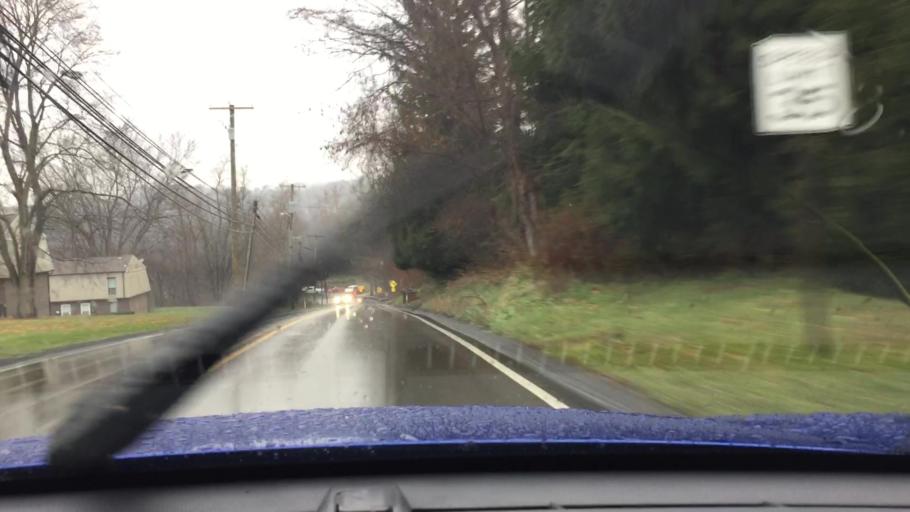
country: US
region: Pennsylvania
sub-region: Washington County
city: Thompsonville
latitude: 40.2759
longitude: -80.1345
